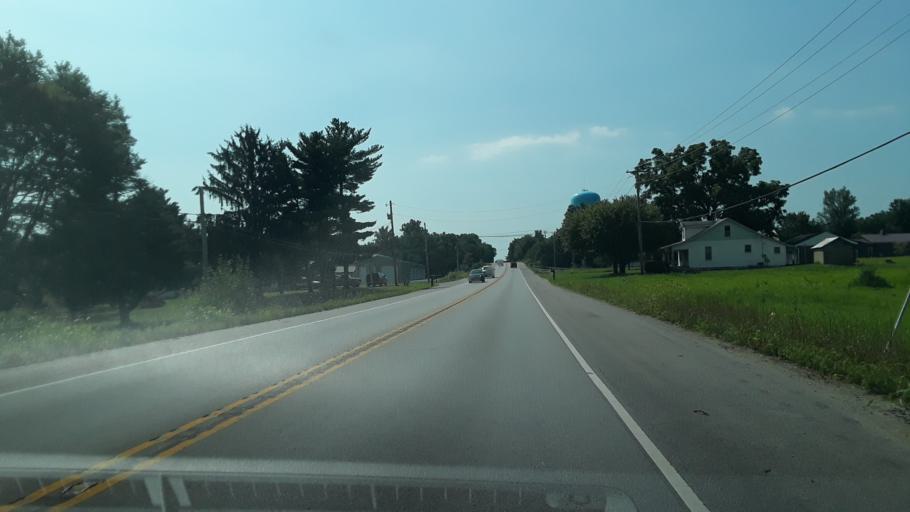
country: US
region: Indiana
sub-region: Clark County
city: Sellersburg
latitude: 38.4240
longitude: -85.8056
